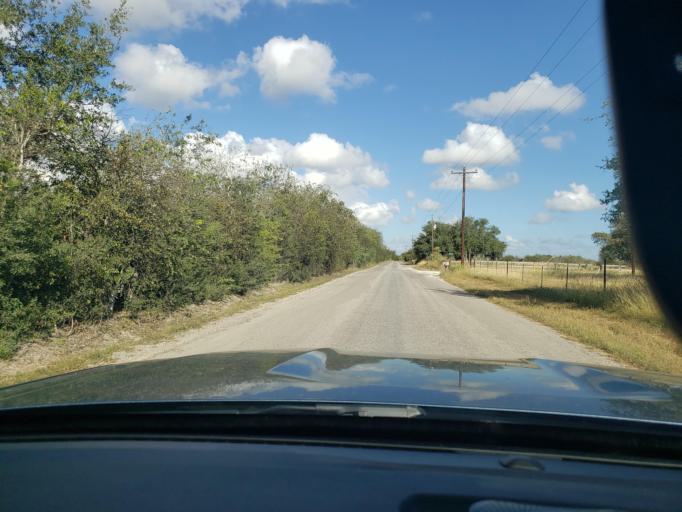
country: US
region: Texas
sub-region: Bee County
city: Beeville
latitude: 28.4447
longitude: -97.7153
